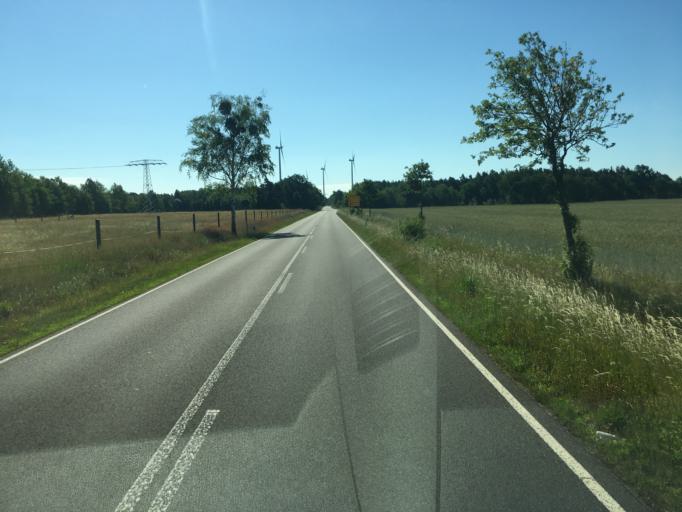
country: DE
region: Brandenburg
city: Welzow
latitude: 51.5540
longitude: 14.1432
